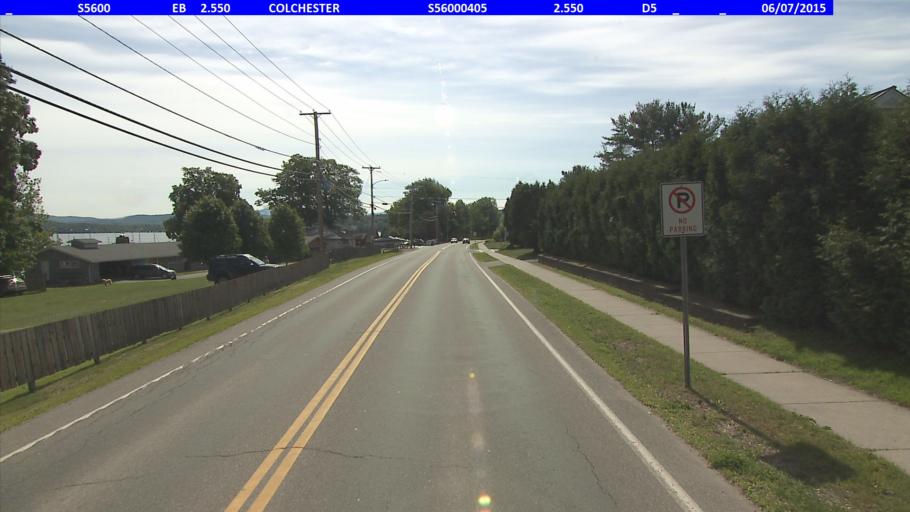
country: US
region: Vermont
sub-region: Chittenden County
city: Winooski
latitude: 44.5499
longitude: -73.2268
